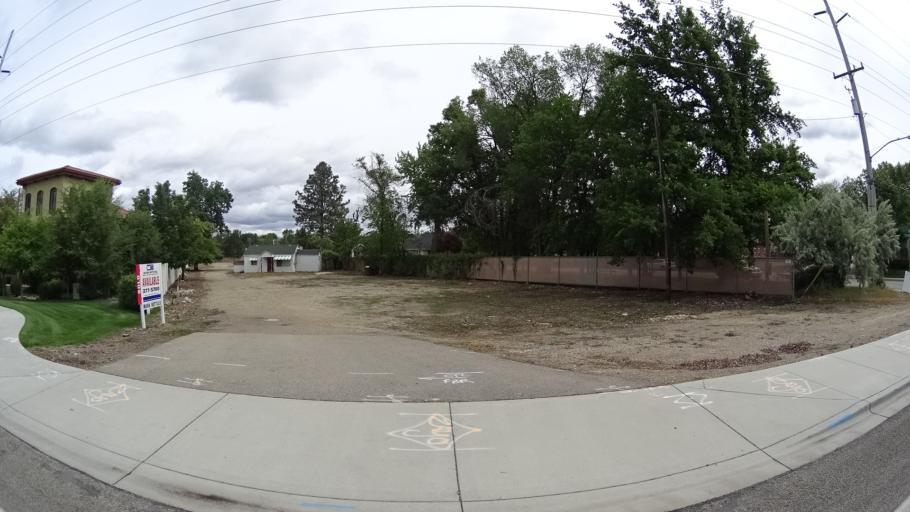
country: US
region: Idaho
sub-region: Ada County
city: Eagle
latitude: 43.6922
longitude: -116.3377
